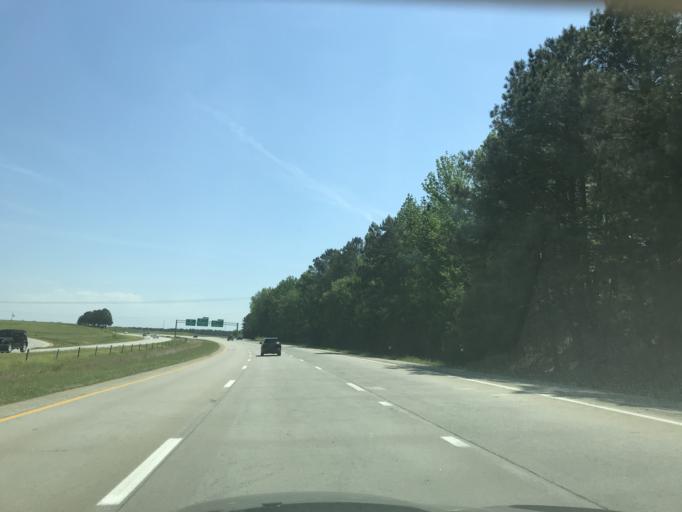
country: US
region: North Carolina
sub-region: Johnston County
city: Benson
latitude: 35.3972
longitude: -78.5226
